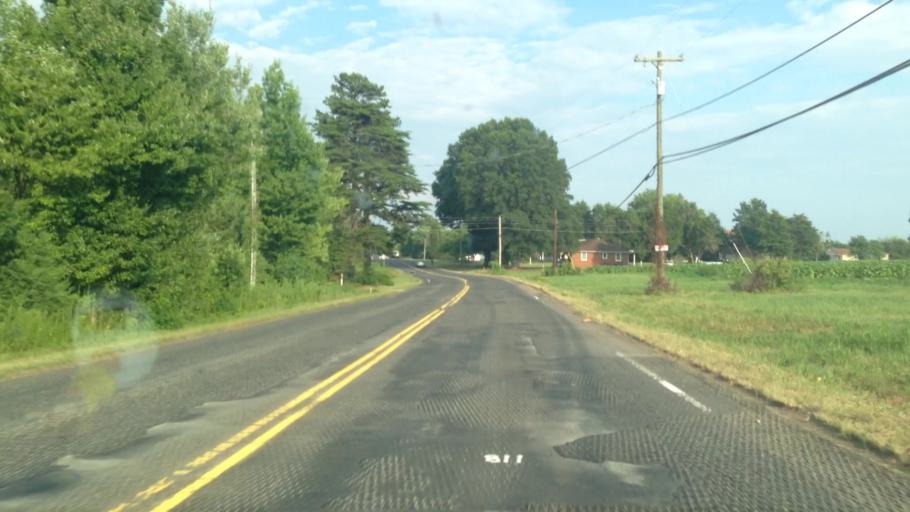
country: US
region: North Carolina
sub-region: Forsyth County
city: Kernersville
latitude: 36.0464
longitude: -80.0600
